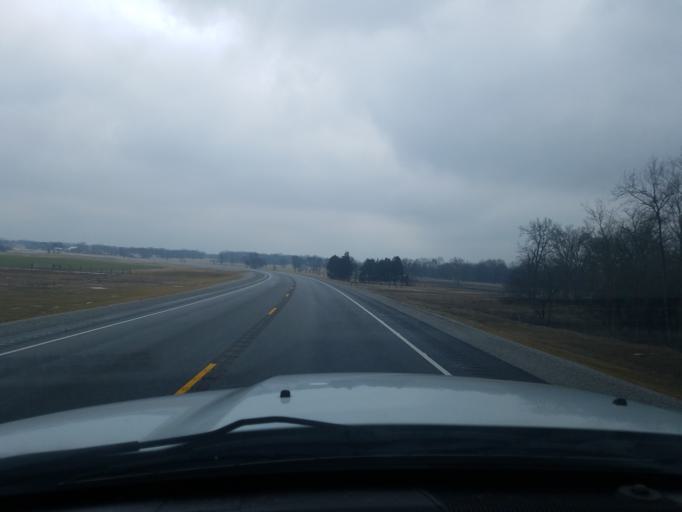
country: US
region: Kentucky
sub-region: Logan County
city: Russellville
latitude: 36.8114
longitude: -86.8986
